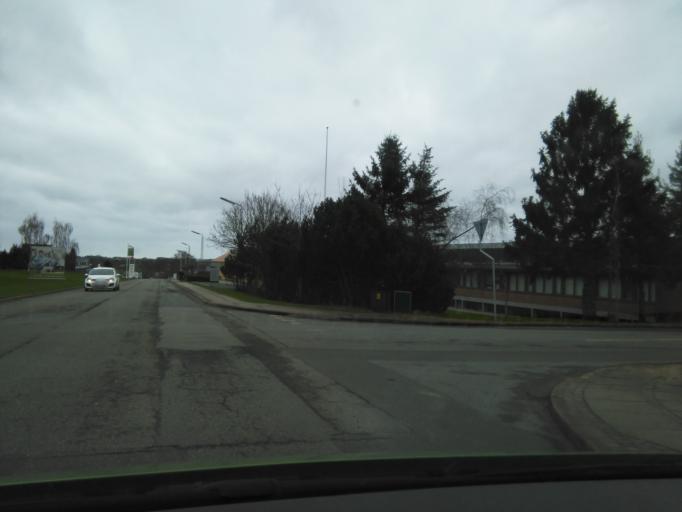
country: DK
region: Central Jutland
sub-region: Odder Kommune
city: Odder
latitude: 55.9851
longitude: 10.1453
